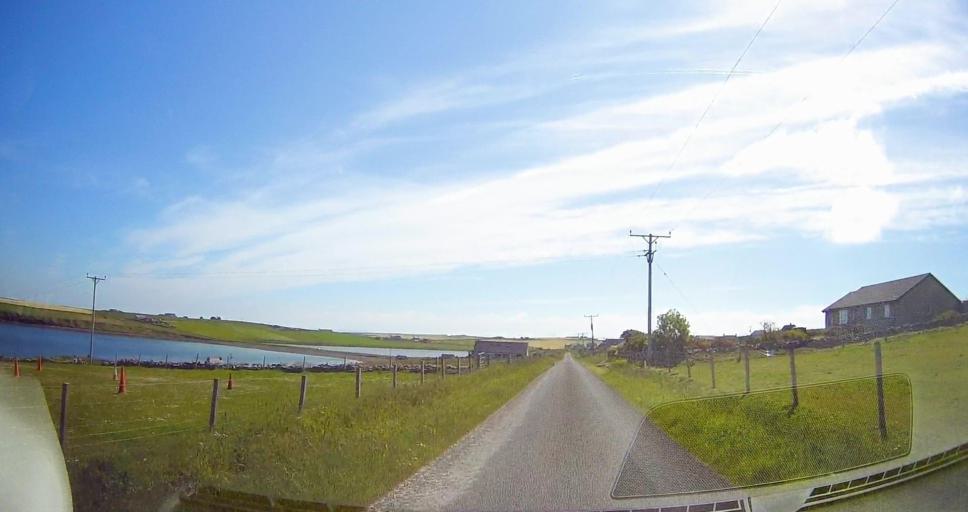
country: GB
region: Scotland
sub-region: Orkney Islands
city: Kirkwall
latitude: 58.8555
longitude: -2.9286
